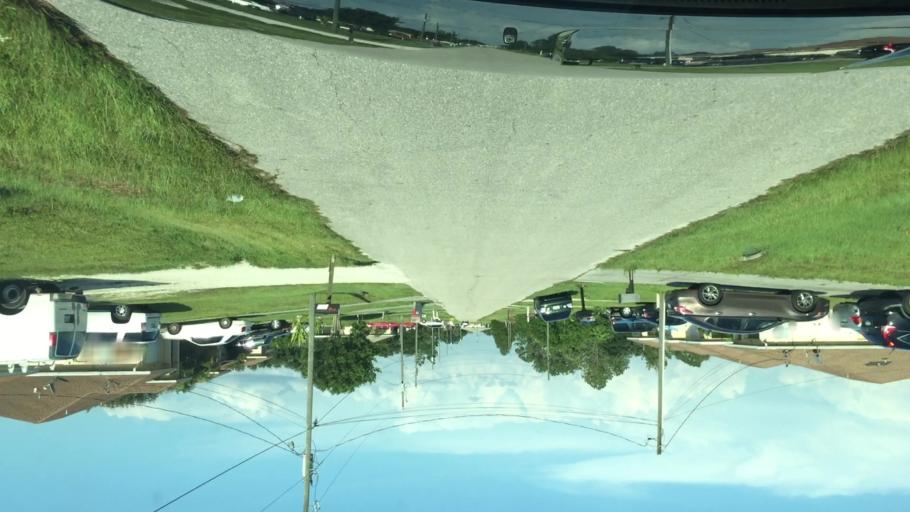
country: US
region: Florida
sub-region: Lee County
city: Gateway
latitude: 26.5905
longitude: -81.7207
